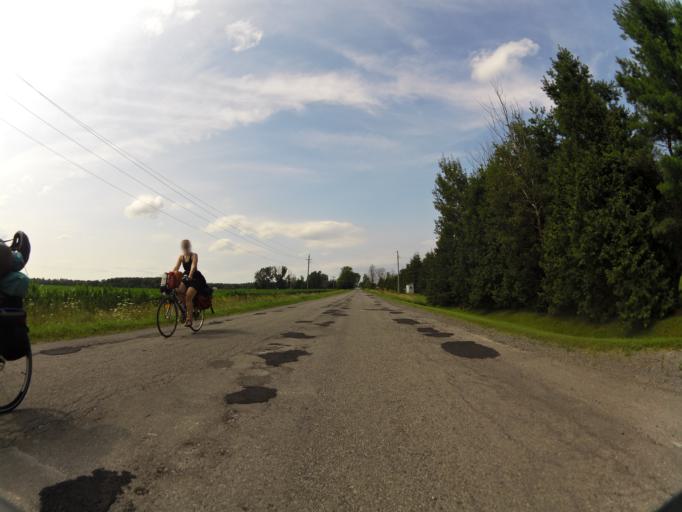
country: CA
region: Ontario
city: Bells Corners
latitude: 45.1120
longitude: -75.5980
